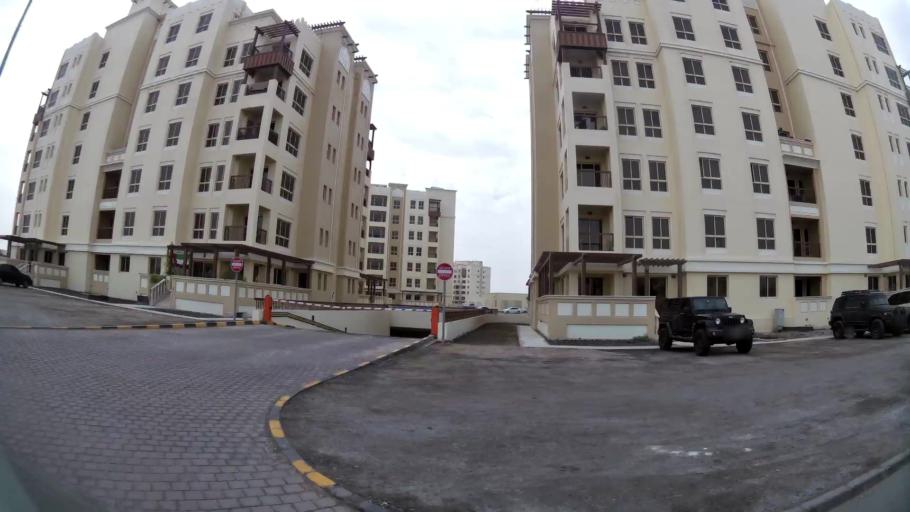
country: AE
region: Abu Dhabi
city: Abu Dhabi
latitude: 24.3137
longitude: 54.6230
